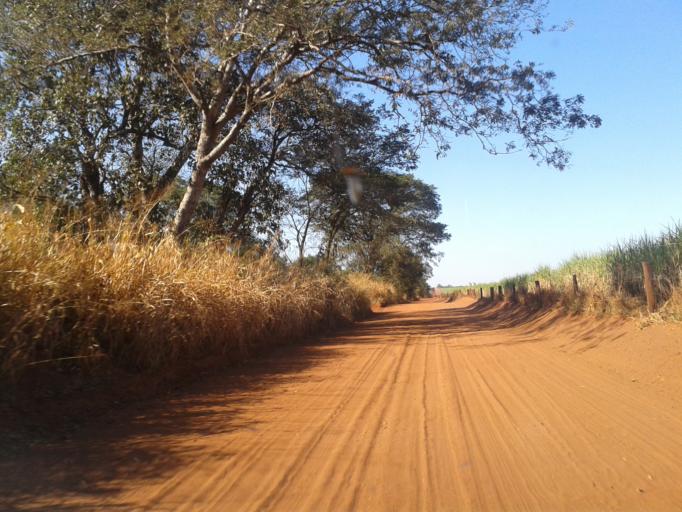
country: BR
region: Minas Gerais
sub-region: Santa Vitoria
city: Santa Vitoria
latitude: -18.8347
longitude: -50.0842
